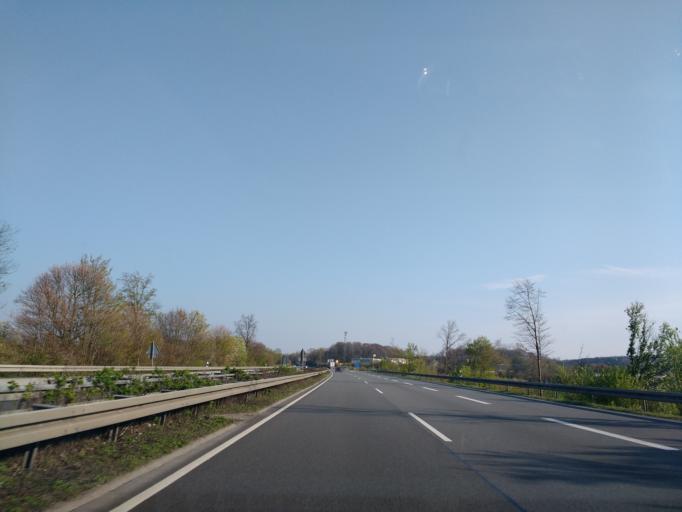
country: DE
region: Lower Saxony
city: Georgsmarienhutte
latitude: 52.2270
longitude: 8.0946
